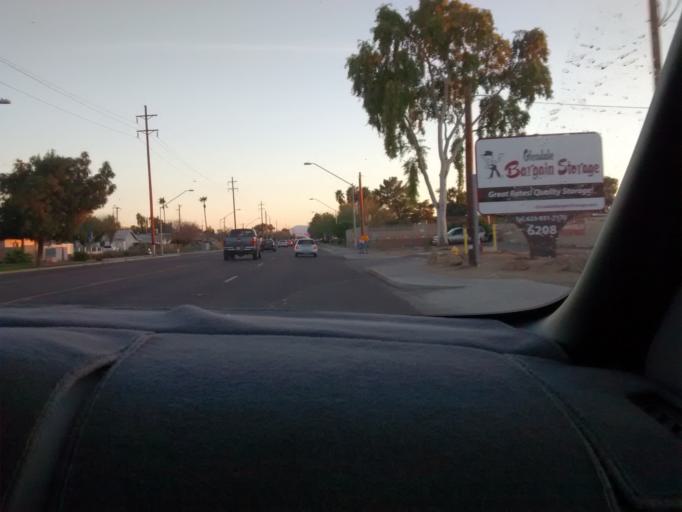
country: US
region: Arizona
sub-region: Maricopa County
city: Glendale
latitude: 33.5281
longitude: -112.2032
